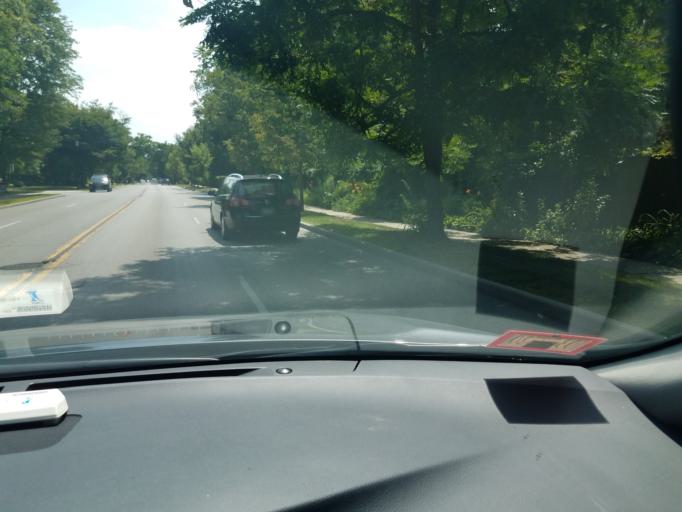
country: US
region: Illinois
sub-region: Cook County
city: Evanston
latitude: 42.0400
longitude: -87.6881
